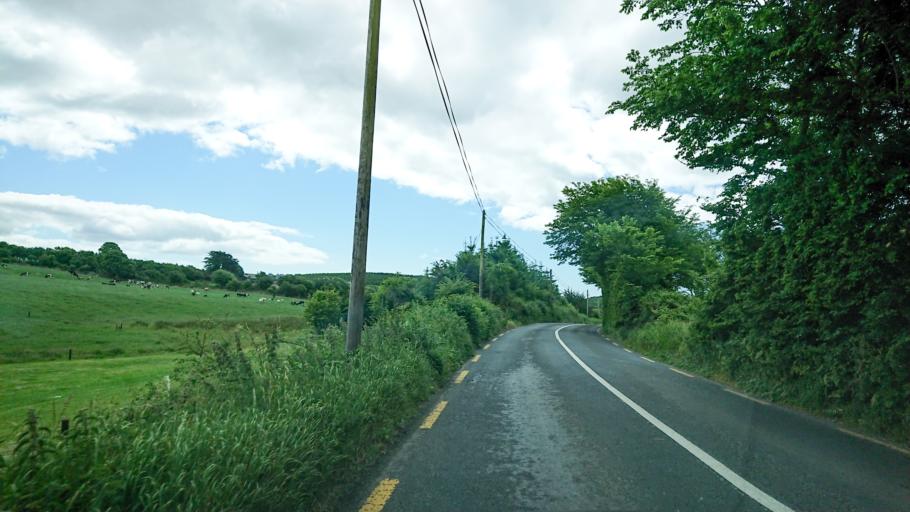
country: IE
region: Munster
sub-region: Waterford
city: Tra Mhor
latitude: 52.1902
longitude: -7.1812
